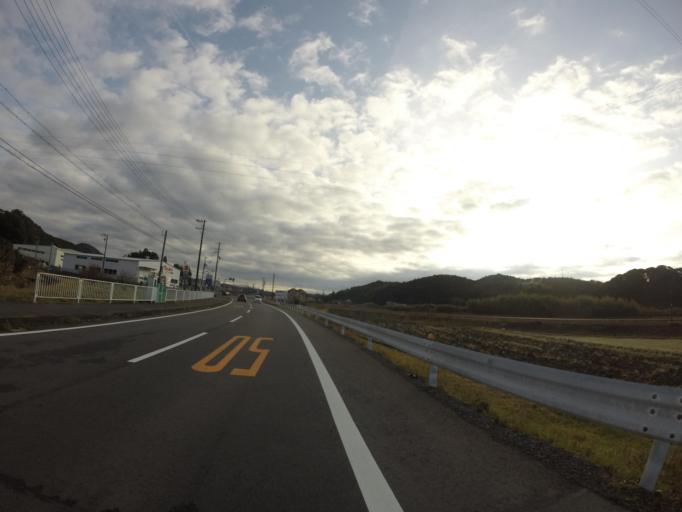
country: JP
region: Shizuoka
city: Hamakita
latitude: 34.8214
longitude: 137.7130
